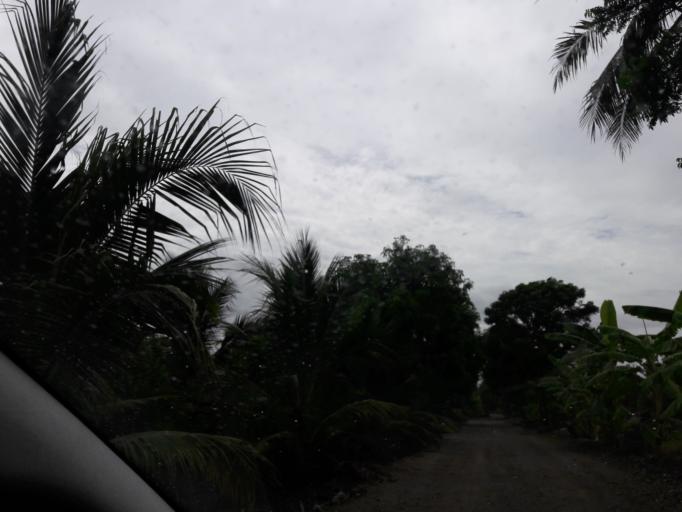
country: TH
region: Ratchaburi
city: Damnoen Saduak
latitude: 13.5261
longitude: 99.9440
